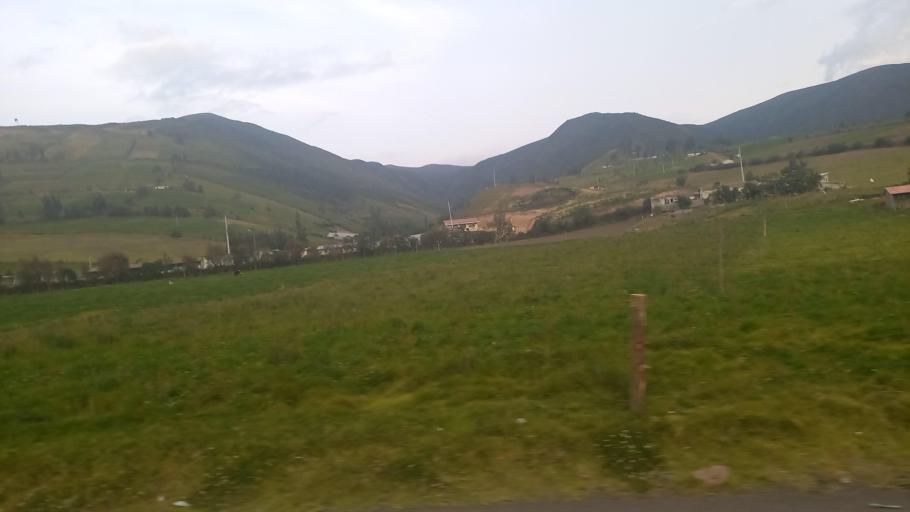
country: EC
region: Pichincha
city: Cayambe
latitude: 0.1124
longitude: -78.0783
